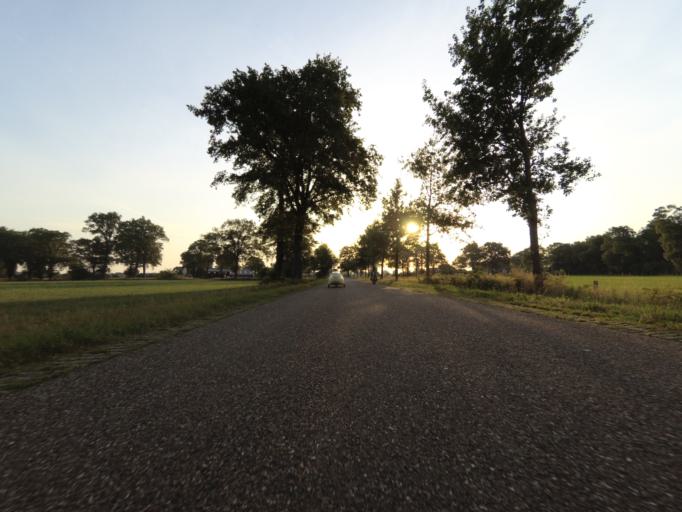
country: NL
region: Overijssel
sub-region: Gemeente Wierden
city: Wierden
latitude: 52.3284
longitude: 6.5069
